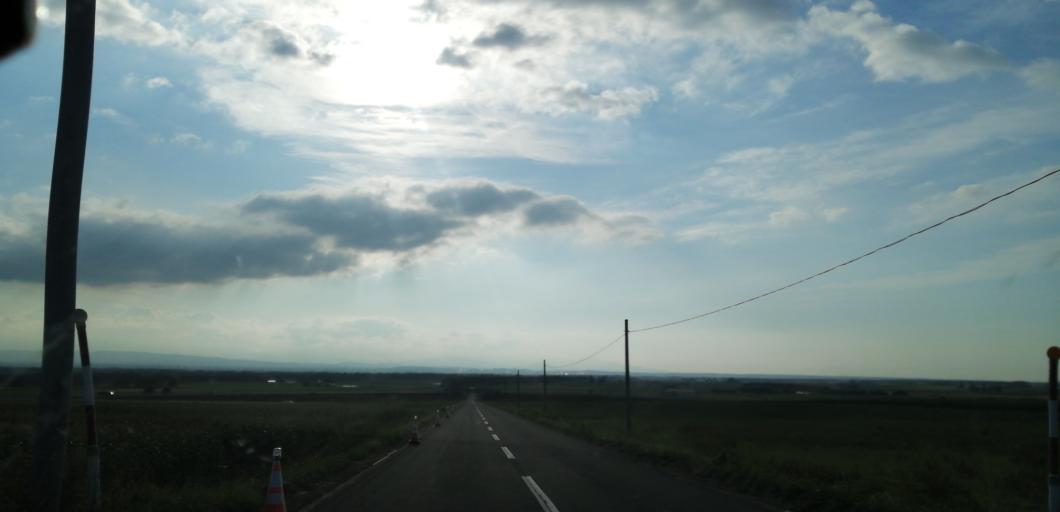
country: JP
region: Hokkaido
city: Chitose
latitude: 42.9353
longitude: 141.7214
